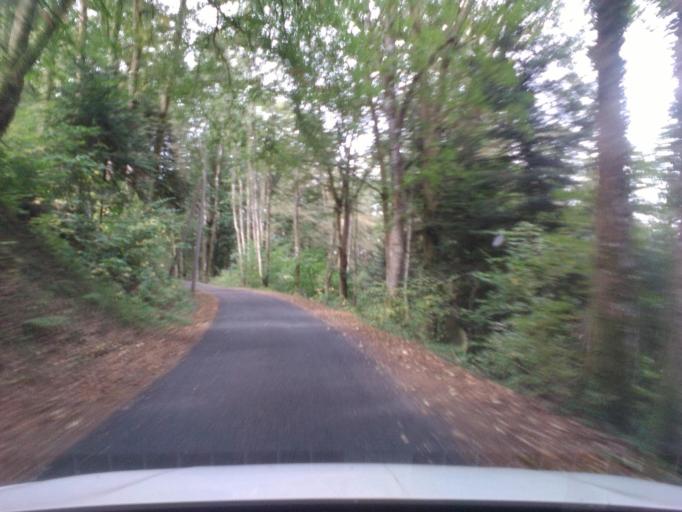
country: FR
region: Lorraine
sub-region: Departement des Vosges
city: Senones
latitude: 48.3643
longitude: 7.0071
